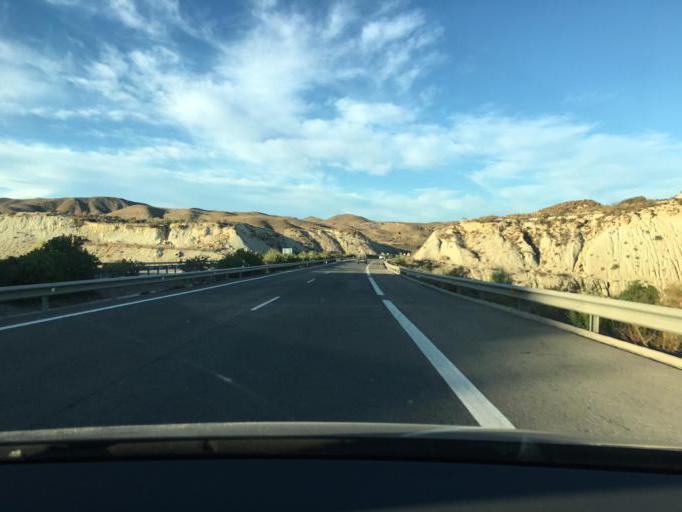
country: ES
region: Andalusia
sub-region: Provincia de Almeria
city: Bedar
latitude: 37.1287
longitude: -2.0124
